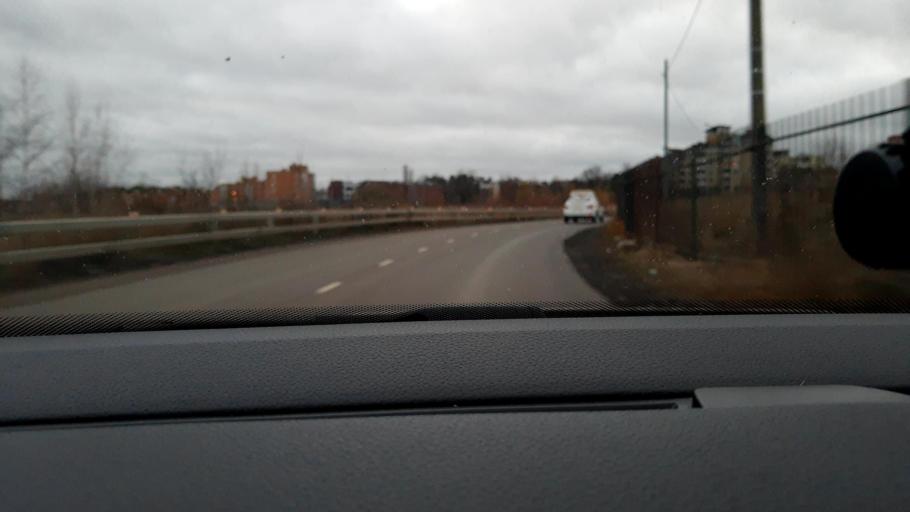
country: RU
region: Moskovskaya
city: Zarech'ye
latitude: 55.6790
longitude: 37.3937
